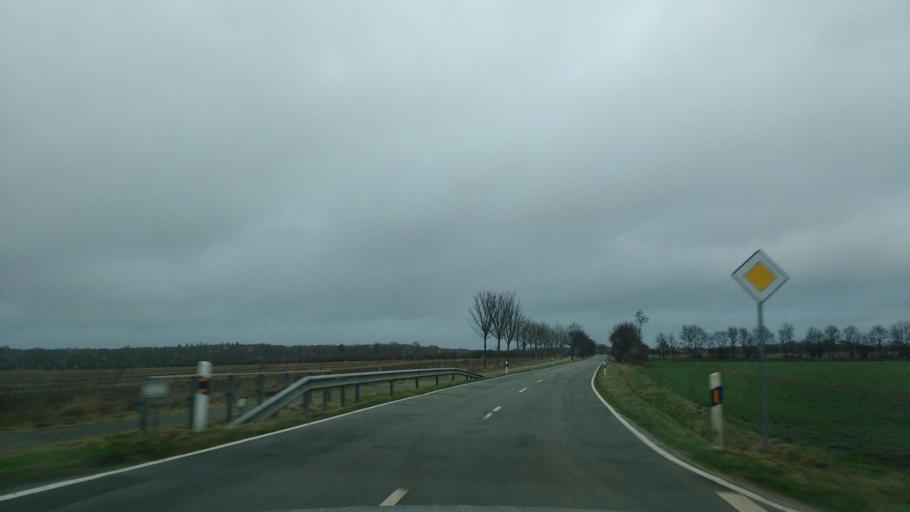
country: DE
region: Schleswig-Holstein
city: Tappendorf
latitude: 54.1011
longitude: 9.6739
